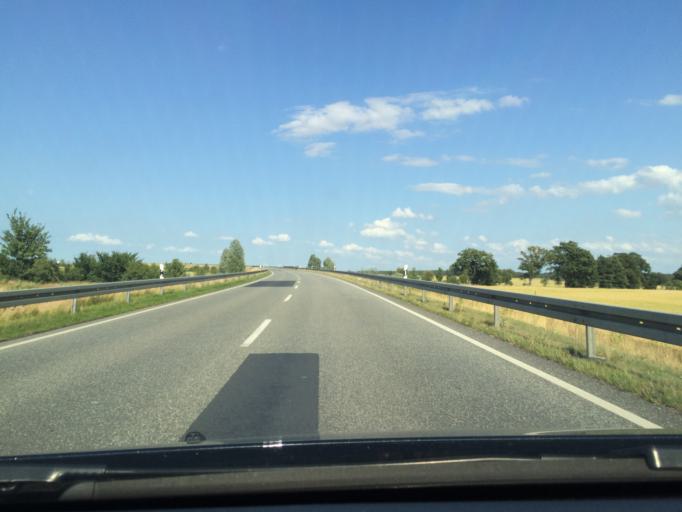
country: DE
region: Mecklenburg-Vorpommern
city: Ribnitz-Damgarten
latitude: 54.2303
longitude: 12.4440
